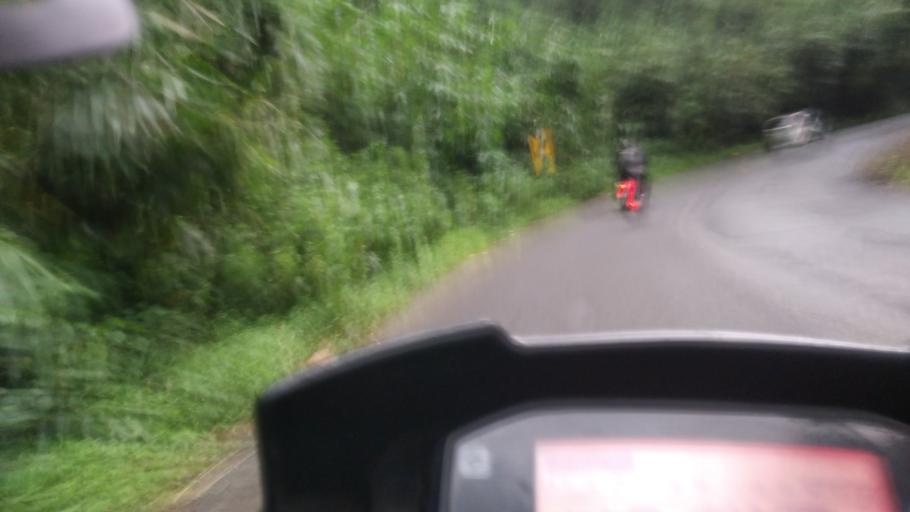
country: IN
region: Kerala
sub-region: Idukki
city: Kuttampuzha
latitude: 10.0655
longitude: 76.7958
